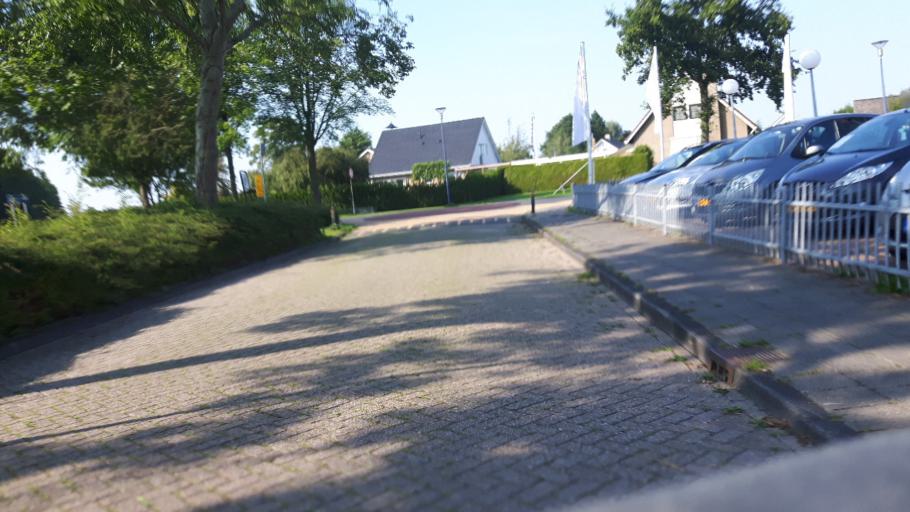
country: NL
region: Friesland
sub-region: Gemeente Franekeradeel
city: Franeker
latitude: 53.1906
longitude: 5.5546
